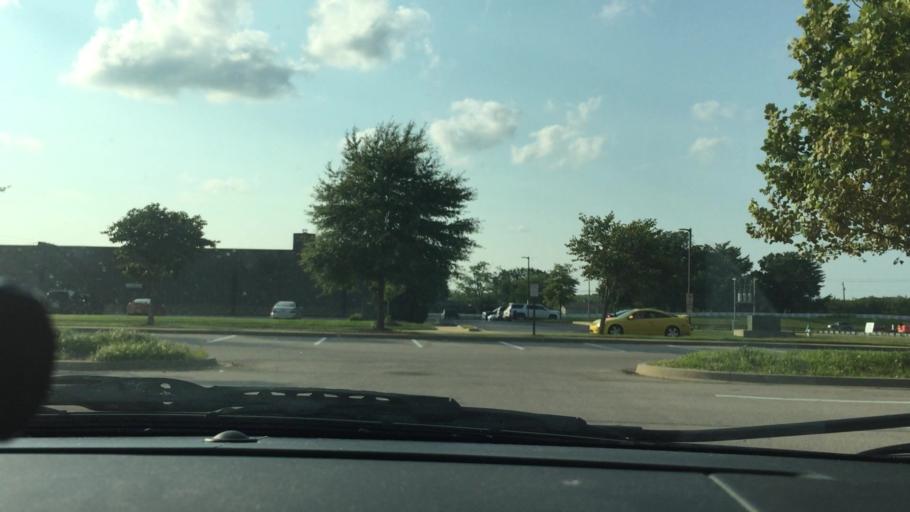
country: US
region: Tennessee
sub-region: Maury County
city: Spring Hill
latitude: 35.7399
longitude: -86.9421
